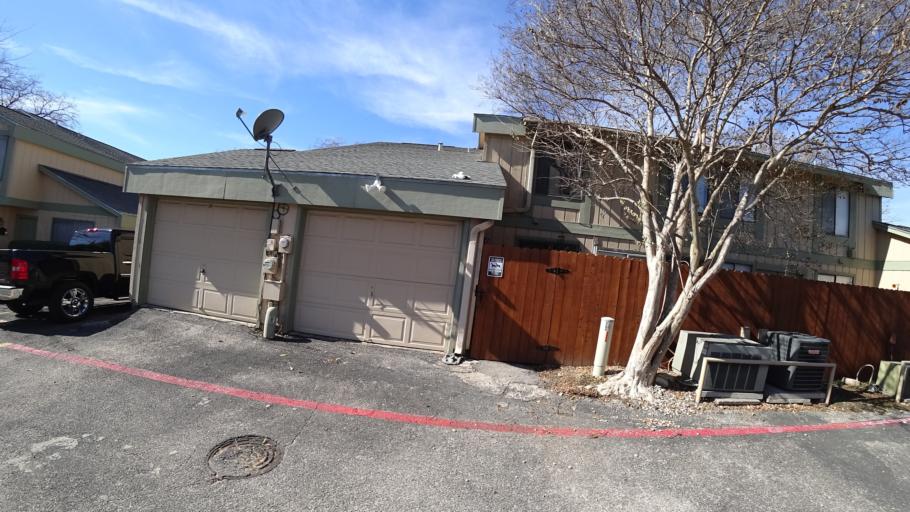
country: US
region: Texas
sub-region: Travis County
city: Wells Branch
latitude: 30.3667
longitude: -97.6982
